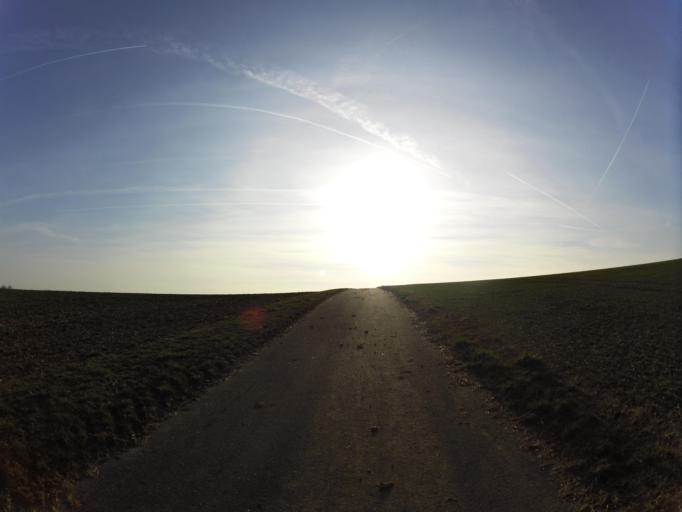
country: DE
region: Bavaria
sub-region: Regierungsbezirk Unterfranken
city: Prosselsheim
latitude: 49.8338
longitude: 10.1457
